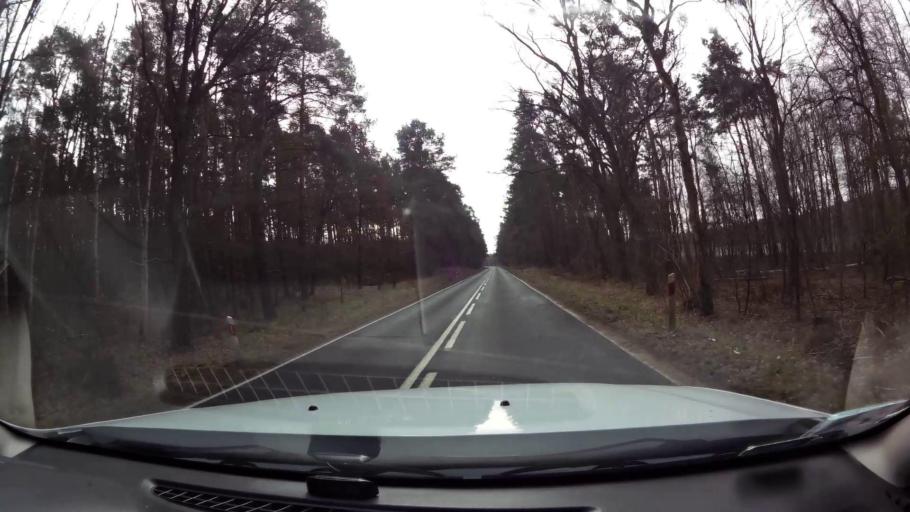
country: PL
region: West Pomeranian Voivodeship
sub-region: Powiat mysliborski
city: Debno
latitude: 52.7645
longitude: 14.6773
